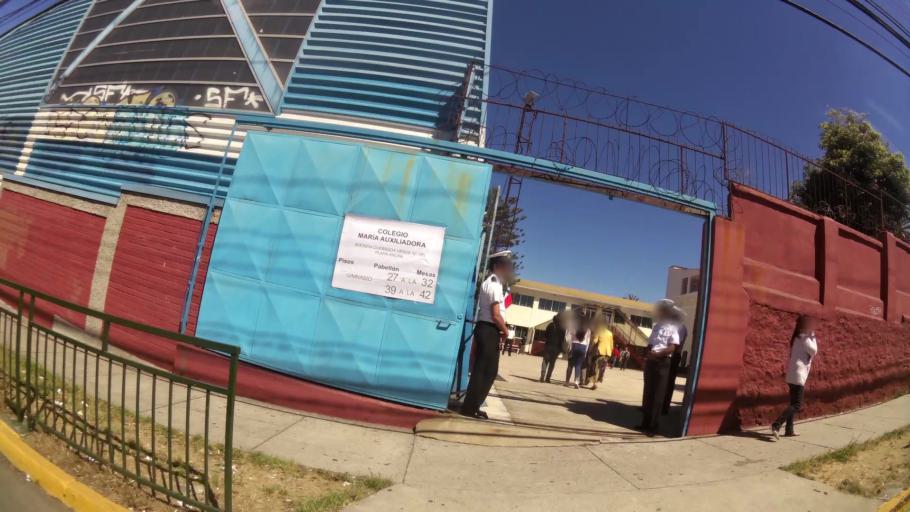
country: CL
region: Valparaiso
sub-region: Provincia de Valparaiso
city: Valparaiso
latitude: -33.0313
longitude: -71.6376
